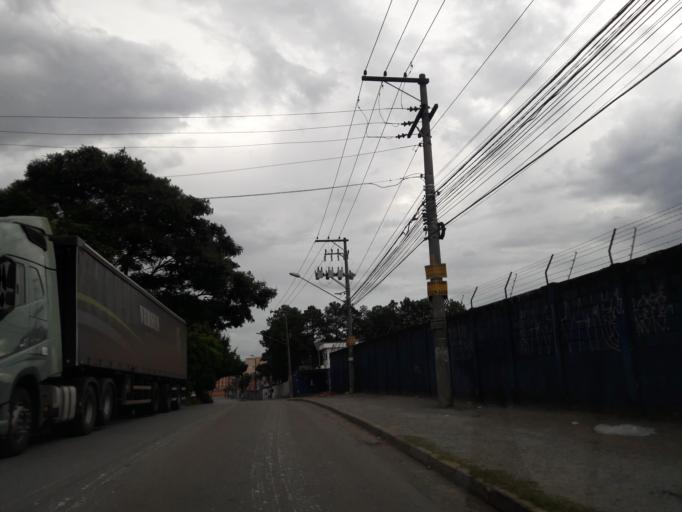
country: BR
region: Sao Paulo
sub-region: Aruja
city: Aruja
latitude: -23.4206
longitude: -46.3950
